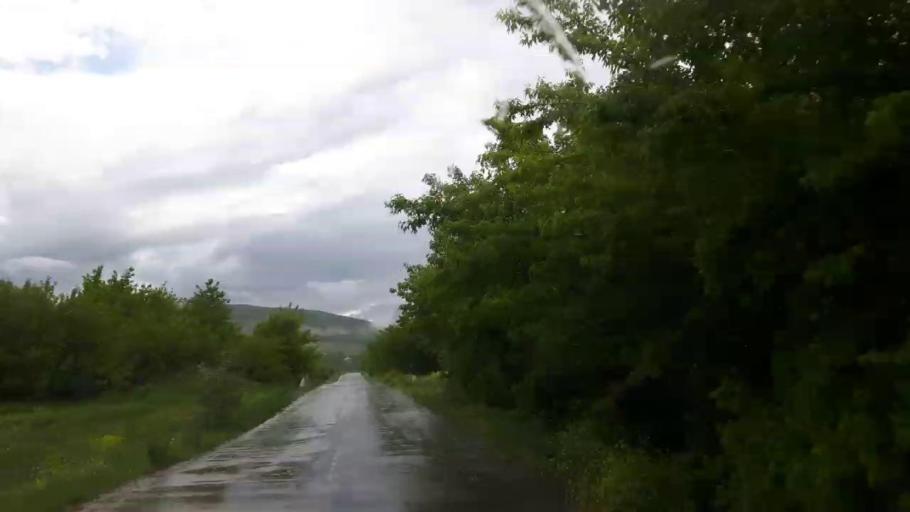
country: GE
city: Agara
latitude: 41.9944
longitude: 43.7439
